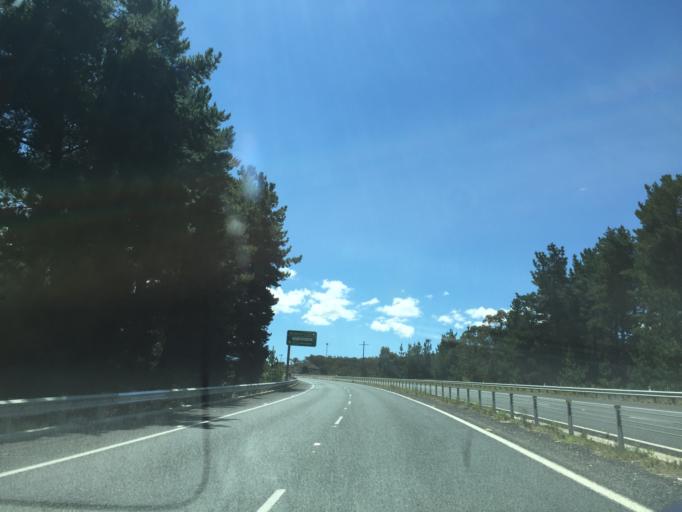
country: AU
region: New South Wales
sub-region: Lithgow
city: Lithgow
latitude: -33.4331
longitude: 150.1120
